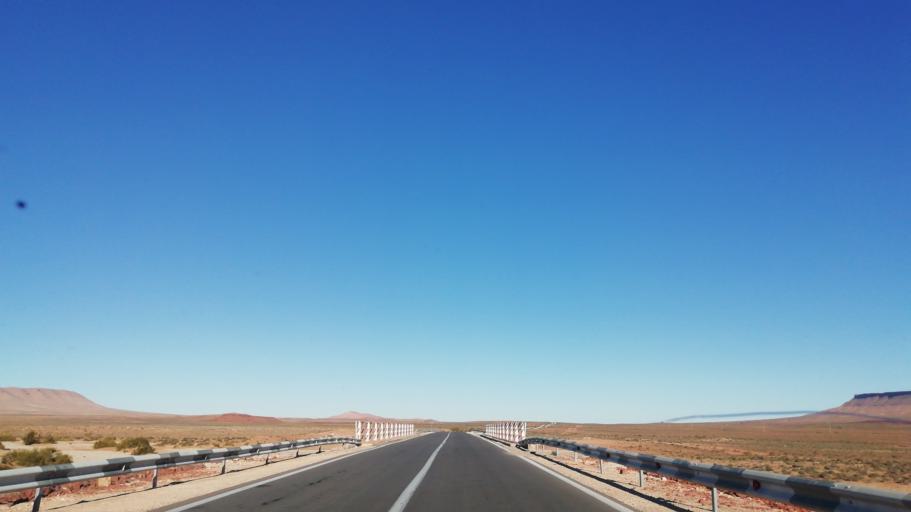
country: DZ
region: El Bayadh
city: El Abiodh Sidi Cheikh
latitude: 33.0847
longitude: 0.1781
